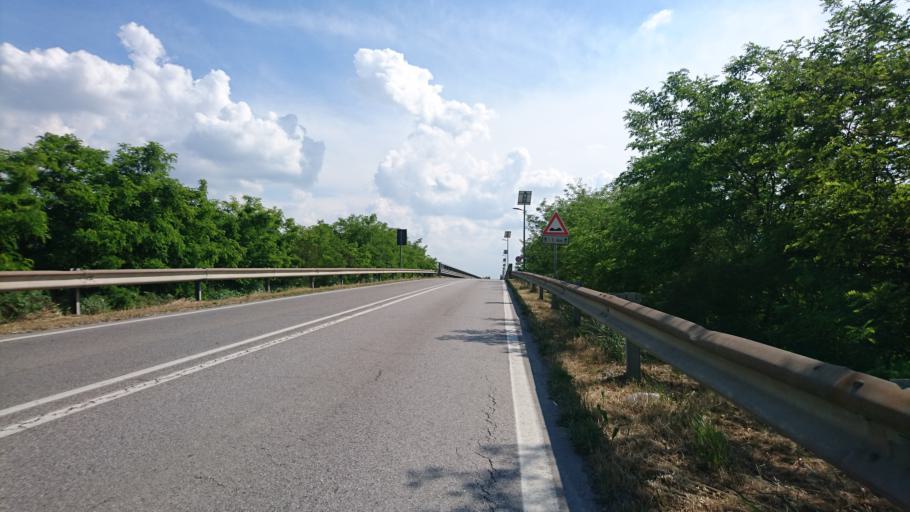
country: IT
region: Veneto
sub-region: Provincia di Rovigo
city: Castelnovo Bariano
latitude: 45.0222
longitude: 11.2930
